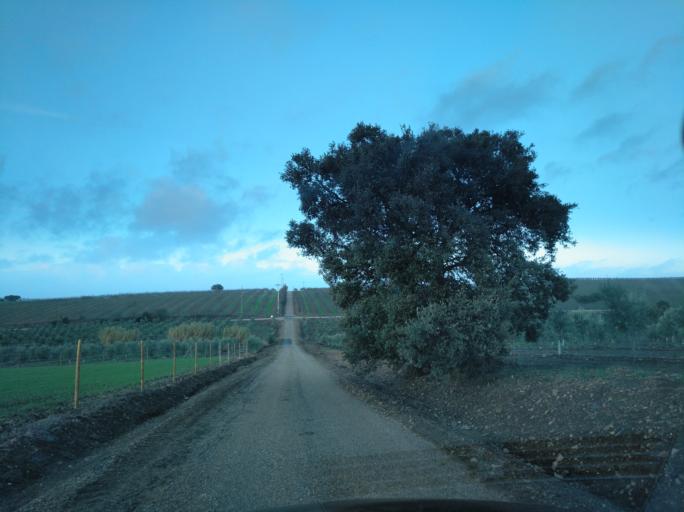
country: PT
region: Portalegre
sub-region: Campo Maior
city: Campo Maior
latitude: 39.0357
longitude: -7.1230
